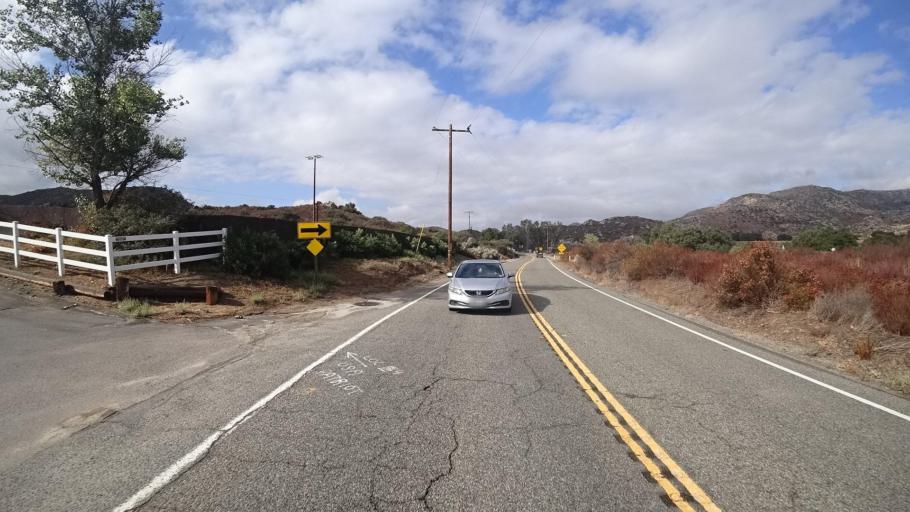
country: US
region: California
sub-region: San Diego County
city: Campo
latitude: 32.5975
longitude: -116.5055
